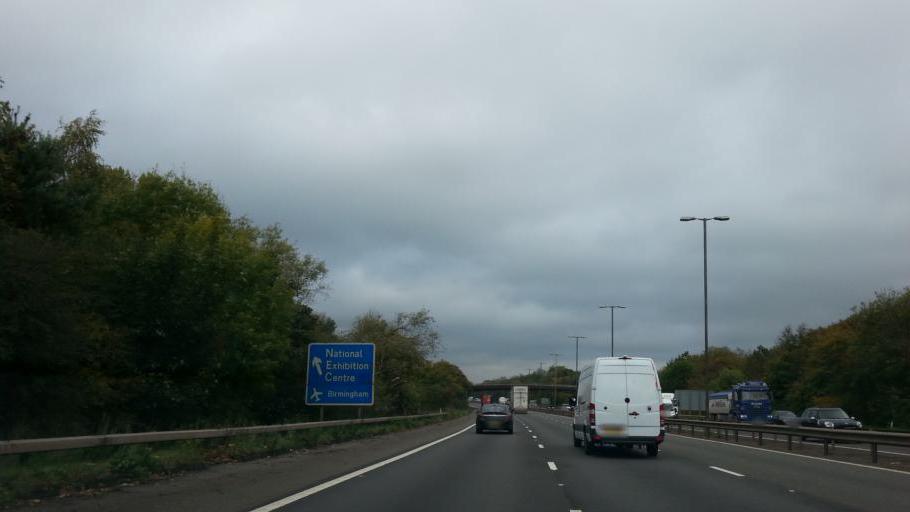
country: GB
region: England
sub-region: Sandwell
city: West Bromwich
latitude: 52.5222
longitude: -1.9704
